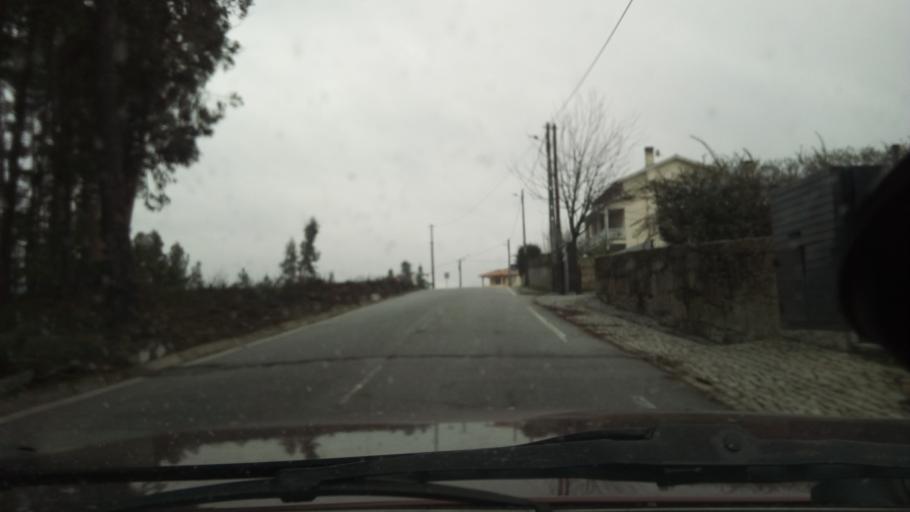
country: PT
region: Viseu
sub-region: Mangualde
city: Mangualde
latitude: 40.5990
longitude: -7.8160
